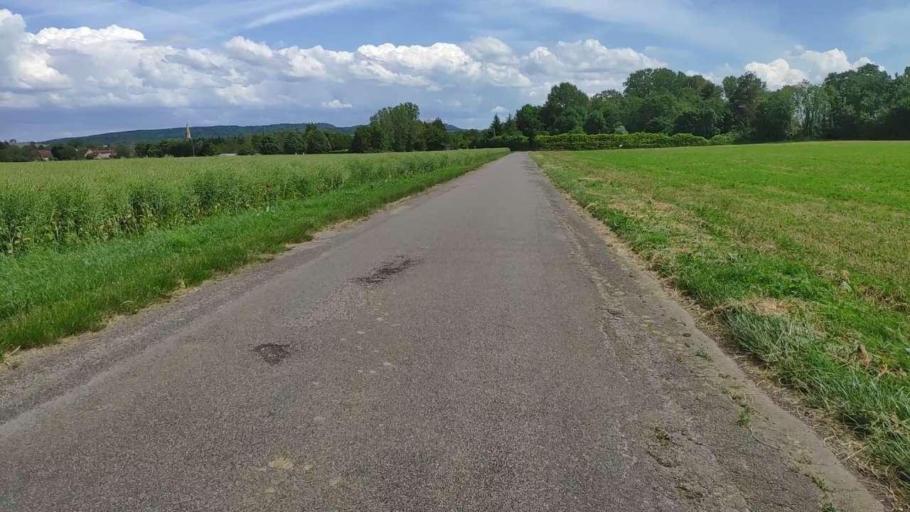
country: FR
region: Franche-Comte
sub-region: Departement du Jura
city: Bletterans
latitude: 46.7468
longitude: 5.4827
